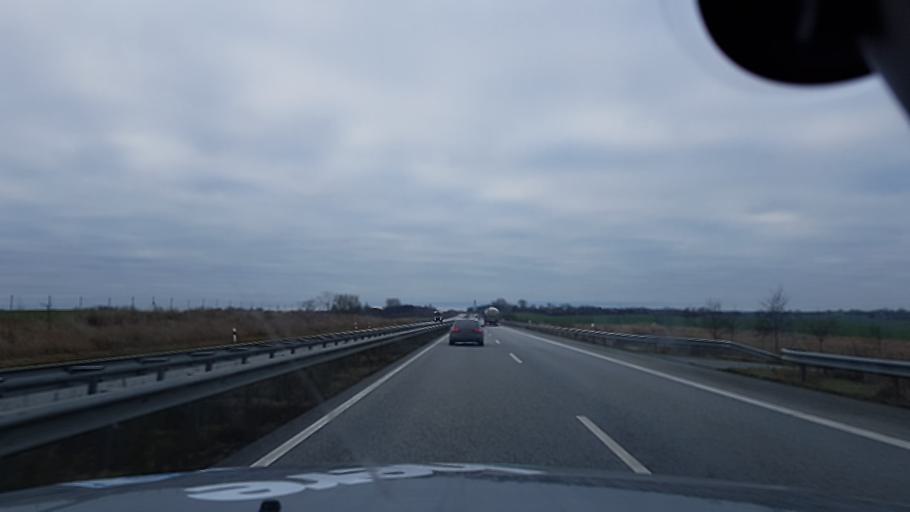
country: DE
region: Schleswig-Holstein
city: Gremersdorf
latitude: 54.3437
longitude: 10.9452
